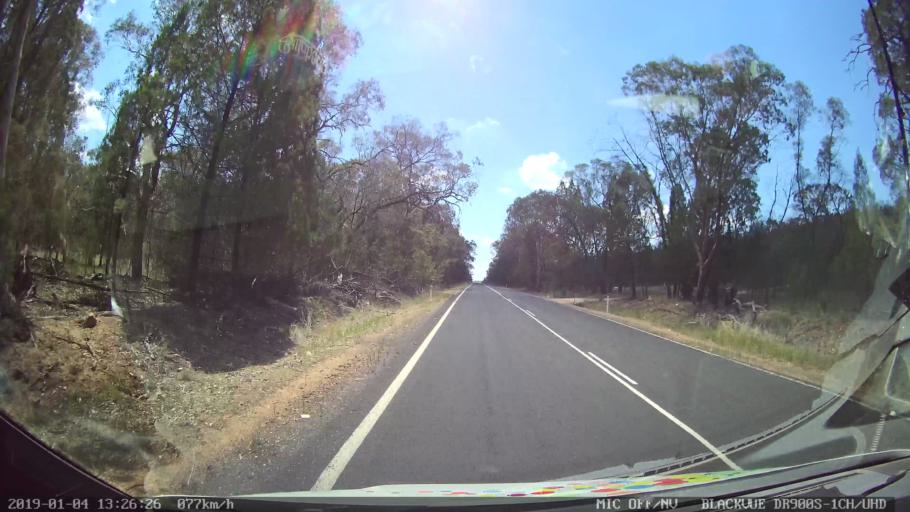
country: AU
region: New South Wales
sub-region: Parkes
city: Peak Hill
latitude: -32.6816
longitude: 148.5576
